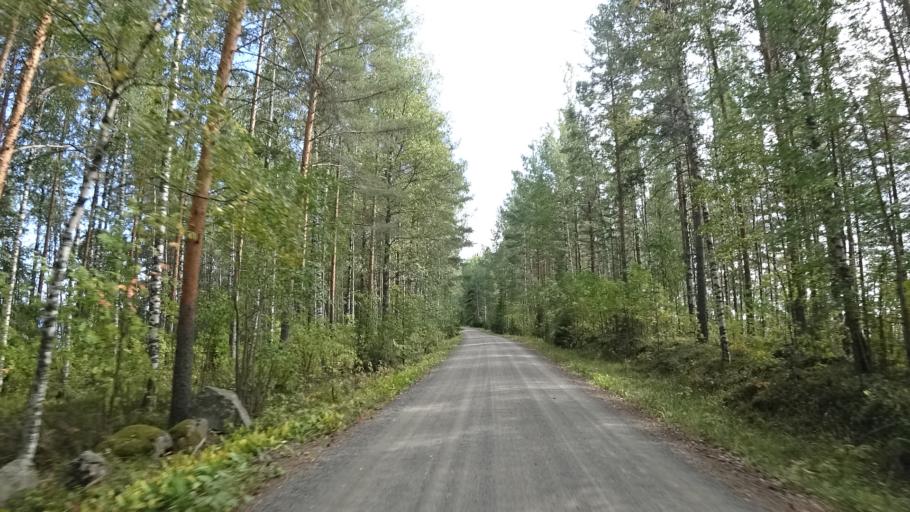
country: FI
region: North Karelia
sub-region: Joensuu
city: Pyhaeselkae
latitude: 62.3875
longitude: 29.7904
